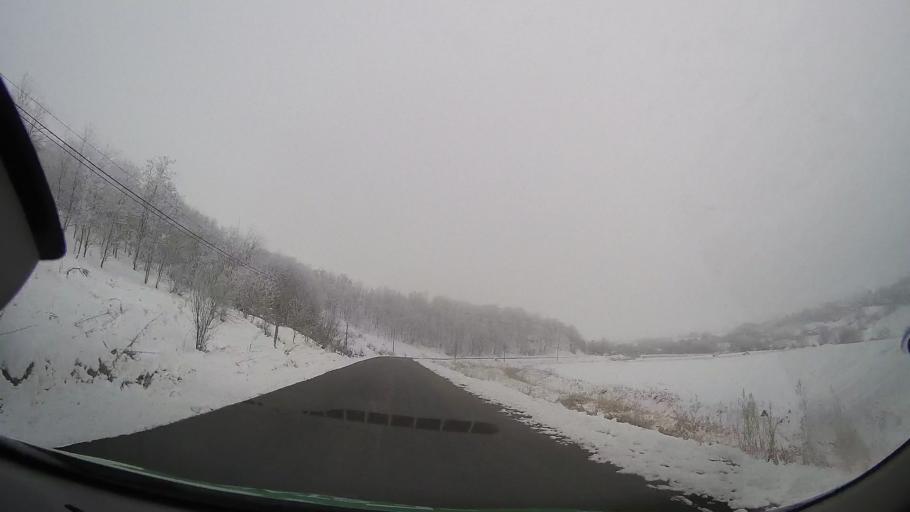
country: RO
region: Bacau
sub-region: Comuna Oncesti
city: Oncesti
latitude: 46.4773
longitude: 27.2572
